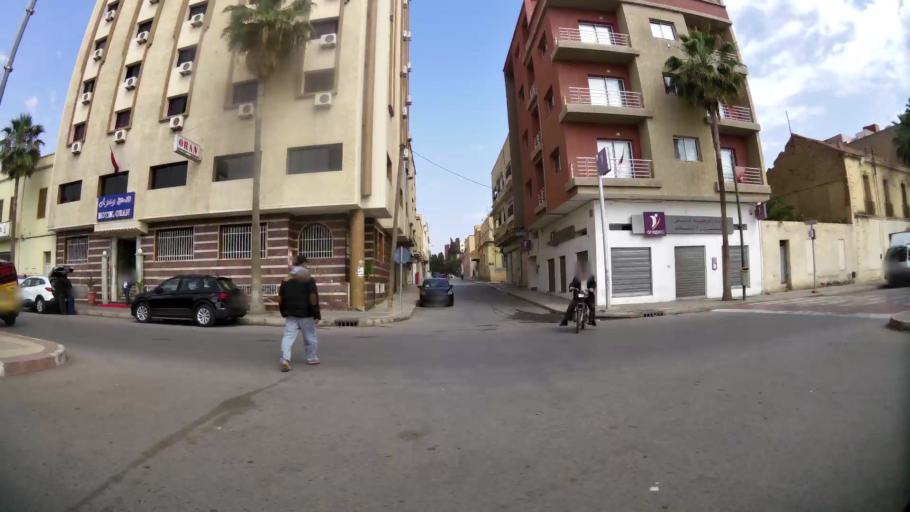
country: MA
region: Oriental
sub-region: Oujda-Angad
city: Oujda
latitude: 34.6866
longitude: -1.9125
